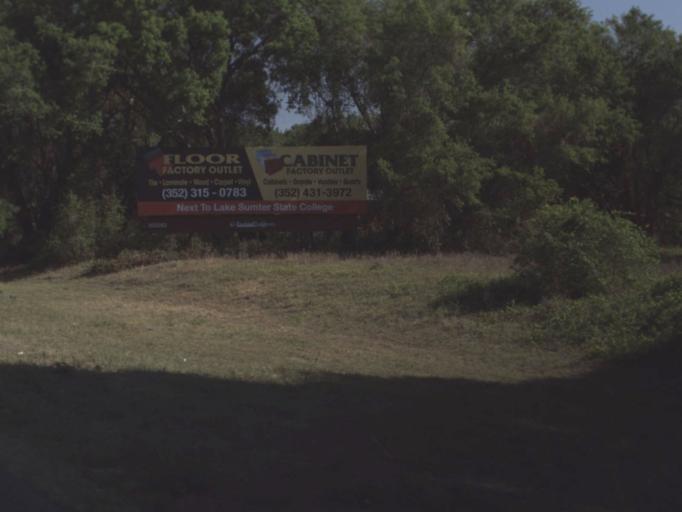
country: US
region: Florida
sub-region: Lake County
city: Yalaha
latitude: 28.6653
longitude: -81.8523
